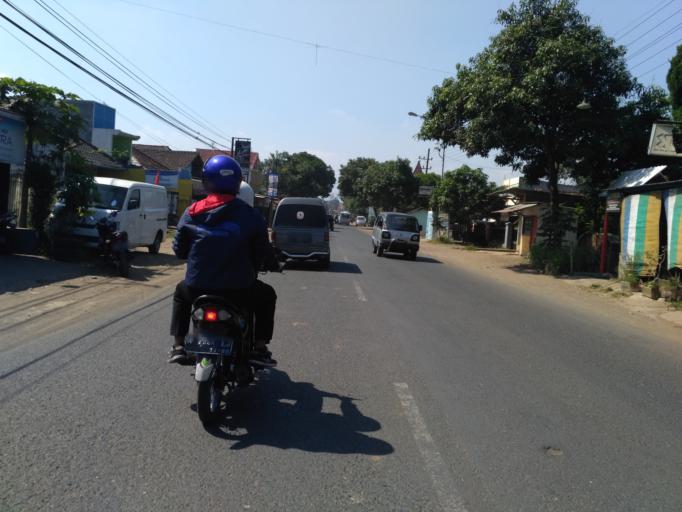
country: ID
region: East Java
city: Tamiajeng
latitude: -7.9543
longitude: 112.7040
